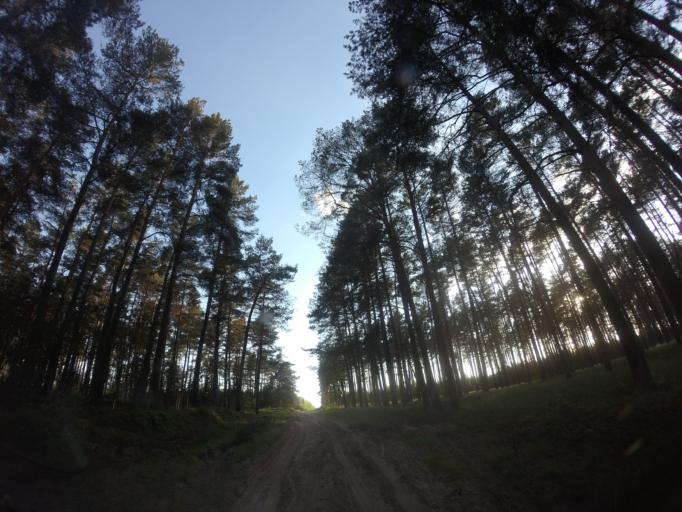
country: PL
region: West Pomeranian Voivodeship
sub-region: Powiat choszczenski
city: Drawno
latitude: 53.1565
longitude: 15.7289
